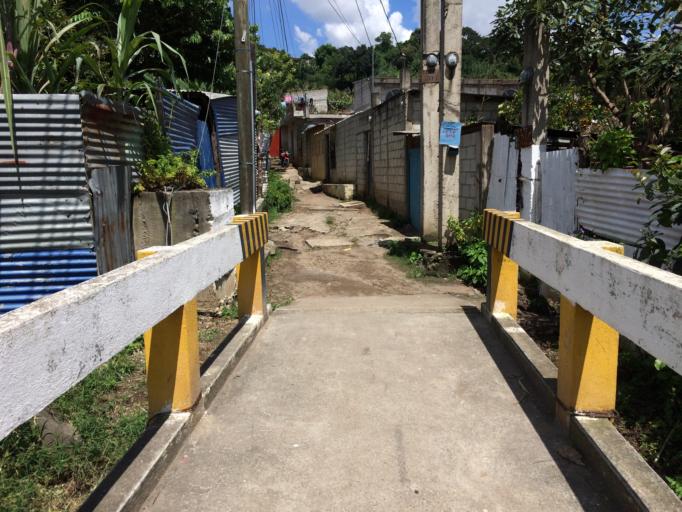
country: GT
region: Guatemala
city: Amatitlan
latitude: 14.4926
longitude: -90.6441
